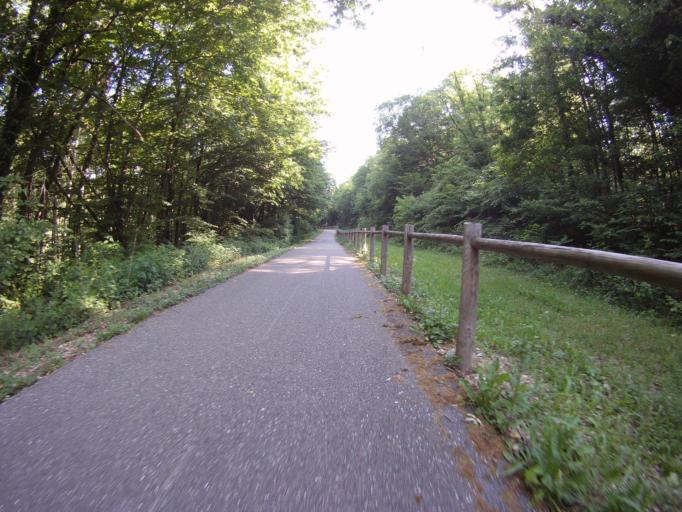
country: FR
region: Lorraine
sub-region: Departement de Meurthe-et-Moselle
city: Champenoux
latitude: 48.7469
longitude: 6.3221
